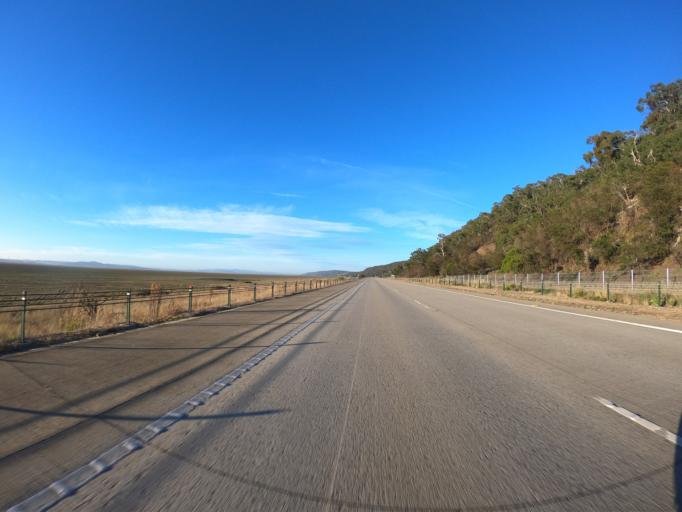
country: AU
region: New South Wales
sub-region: Yass Valley
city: Gundaroo
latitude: -35.0515
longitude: 149.3757
